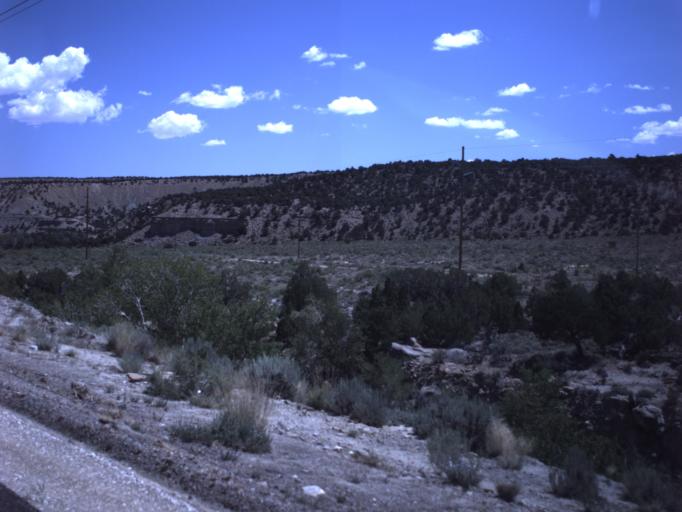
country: US
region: Utah
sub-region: Emery County
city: Orangeville
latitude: 39.2697
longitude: -111.1486
